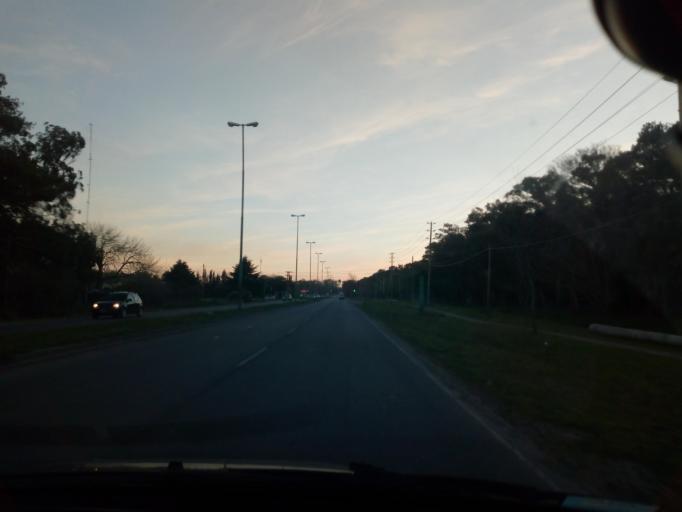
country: AR
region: Buenos Aires
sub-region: Partido de Ensenada
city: Ensenada
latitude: -34.8863
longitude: -57.9300
